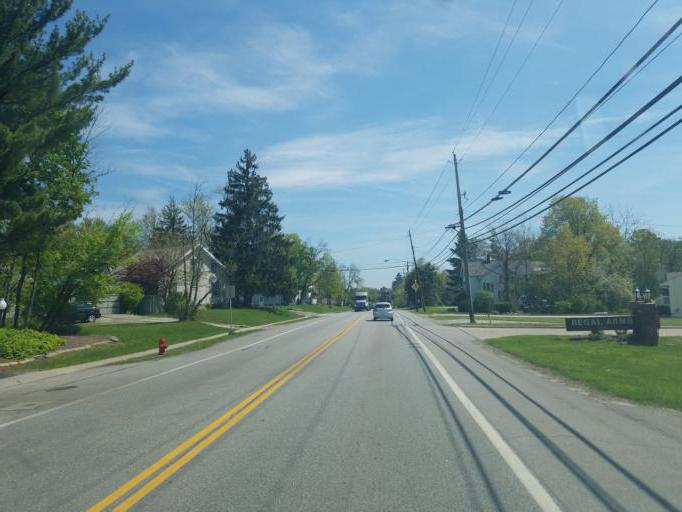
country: US
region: Ohio
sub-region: Medina County
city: Medina
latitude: 41.1321
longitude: -81.8715
